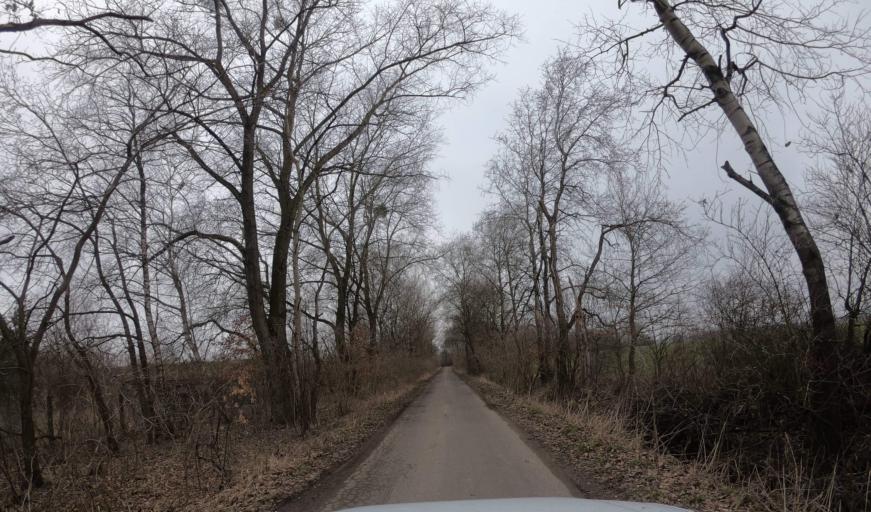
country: PL
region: West Pomeranian Voivodeship
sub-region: Powiat gryficki
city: Ploty
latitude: 53.8593
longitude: 15.2622
